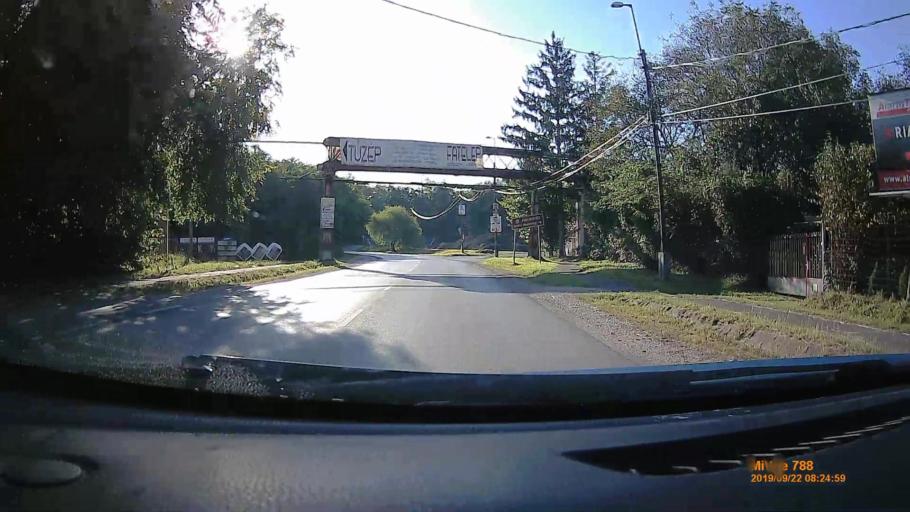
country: HU
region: Borsod-Abauj-Zemplen
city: Miskolc
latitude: 48.0880
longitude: 20.7147
